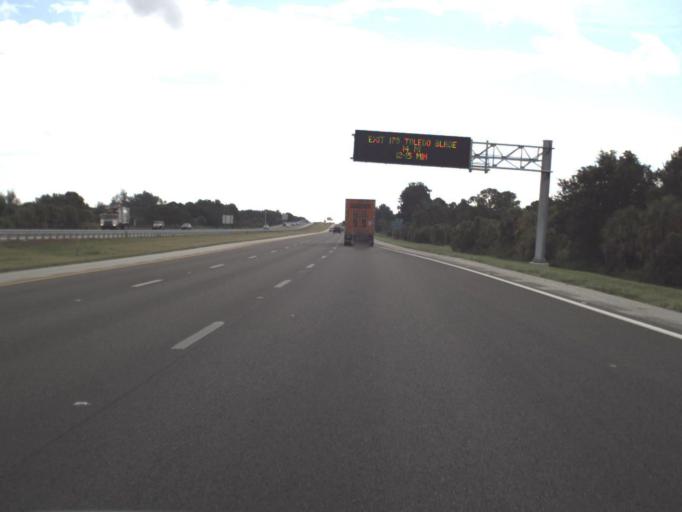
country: US
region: Florida
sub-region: Sarasota County
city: Plantation
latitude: 27.1092
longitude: -82.3769
